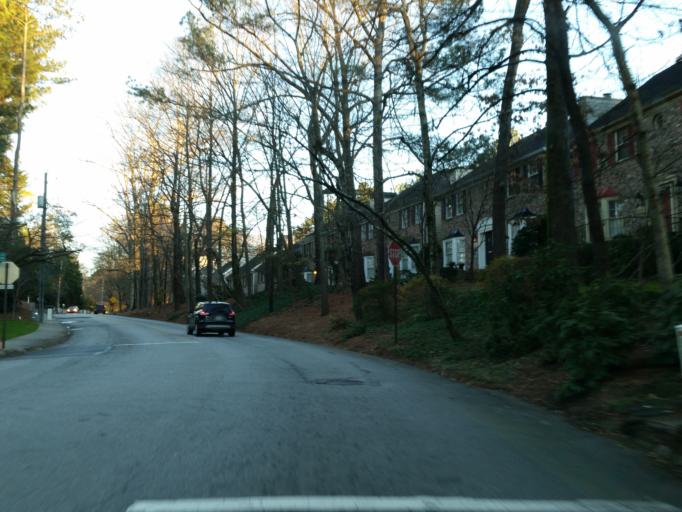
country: US
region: Georgia
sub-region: Cobb County
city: Vinings
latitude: 33.8205
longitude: -84.4363
